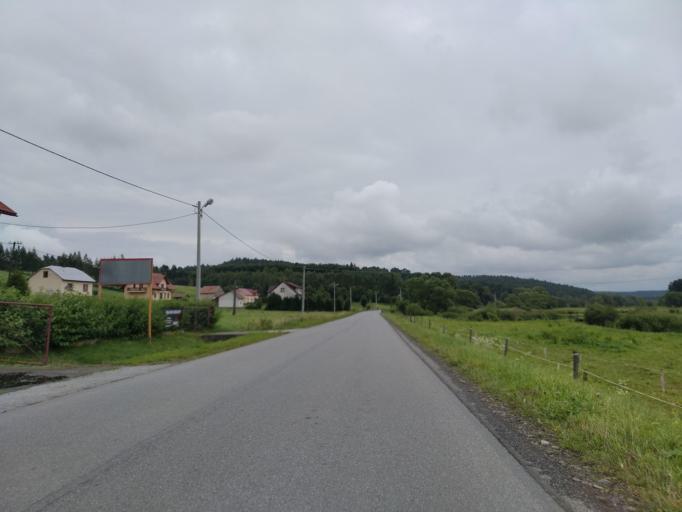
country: PL
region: Subcarpathian Voivodeship
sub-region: Powiat przemyski
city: Bircza
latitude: 49.6944
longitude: 22.3854
